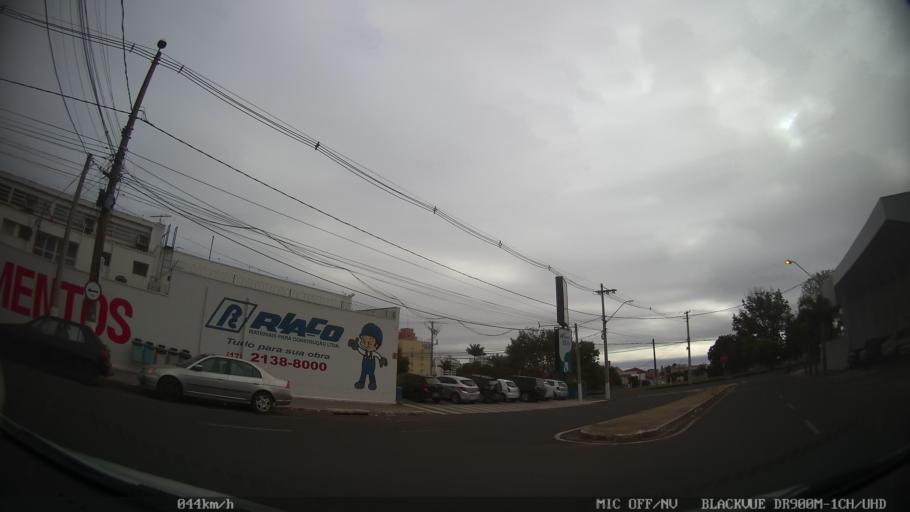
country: BR
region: Sao Paulo
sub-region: Sao Jose Do Rio Preto
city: Sao Jose do Rio Preto
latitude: -20.8245
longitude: -49.3822
